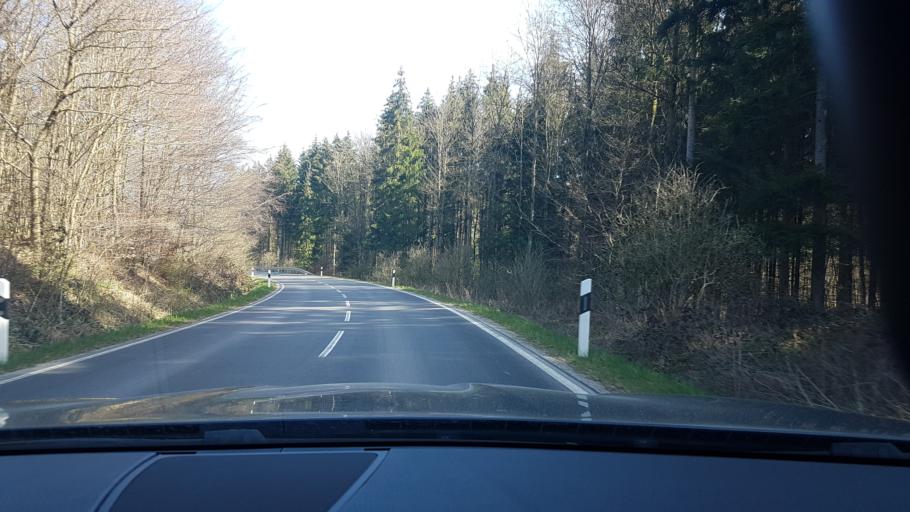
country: DE
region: Lower Saxony
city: Coppenbrugge
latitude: 52.1505
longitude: 9.6004
